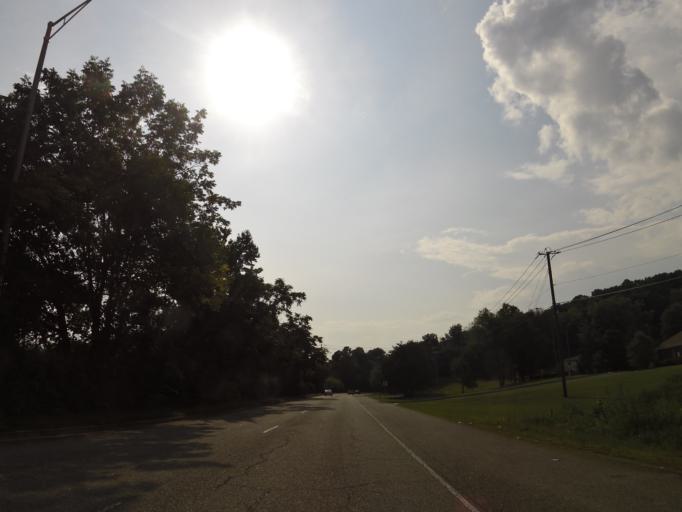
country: US
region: Tennessee
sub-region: Knox County
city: Knoxville
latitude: 36.0316
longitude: -83.8817
